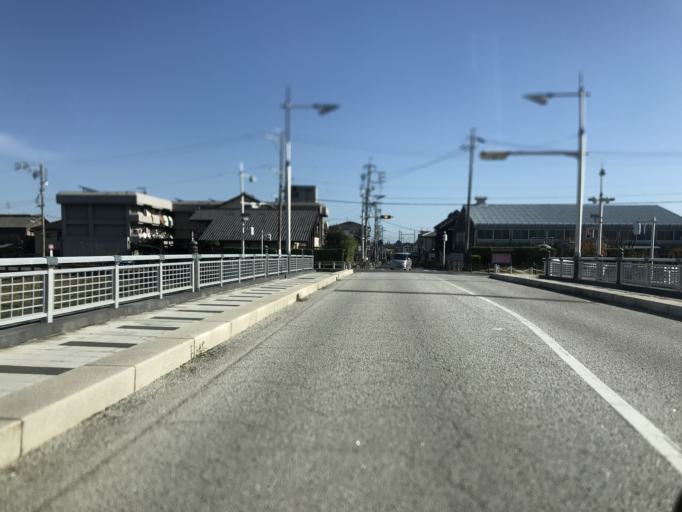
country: JP
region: Aichi
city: Inazawa
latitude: 35.2151
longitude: 136.8403
